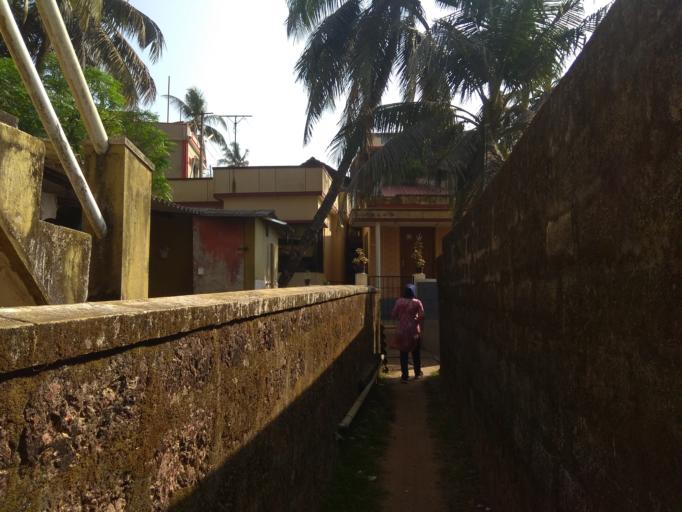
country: IN
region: Karnataka
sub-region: Dakshina Kannada
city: Mangalore
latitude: 12.9321
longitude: 74.8561
